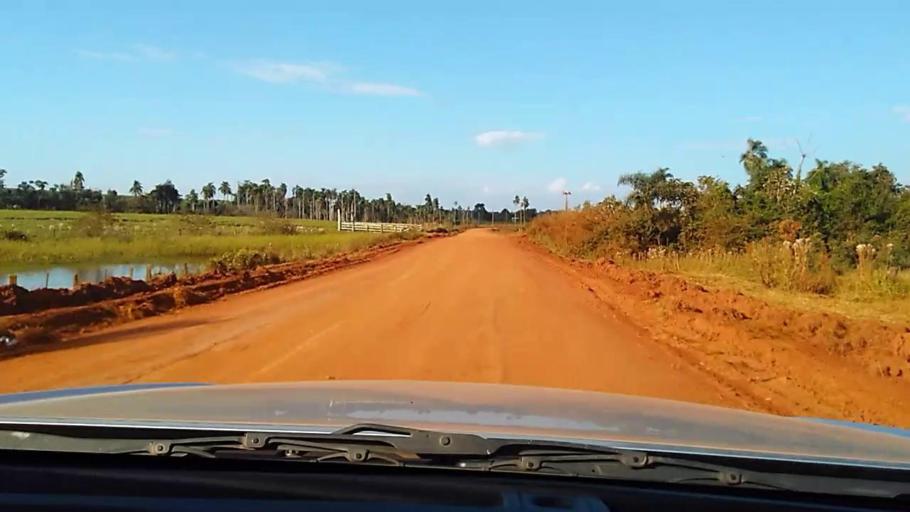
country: PY
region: Alto Parana
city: Doctor Juan Leon Mallorquin
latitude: -25.7028
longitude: -55.3819
